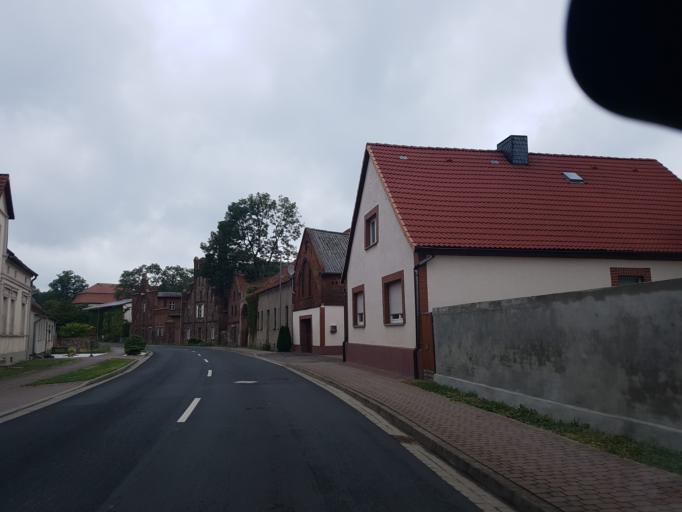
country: DE
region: Saxony-Anhalt
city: Tucheim
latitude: 52.3154
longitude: 12.1167
